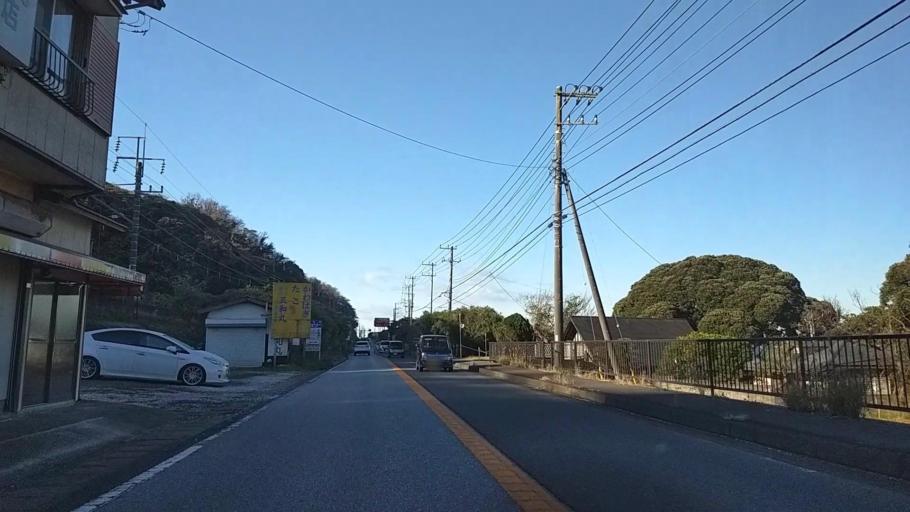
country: JP
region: Chiba
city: Futtsu
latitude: 35.2146
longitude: 139.8566
